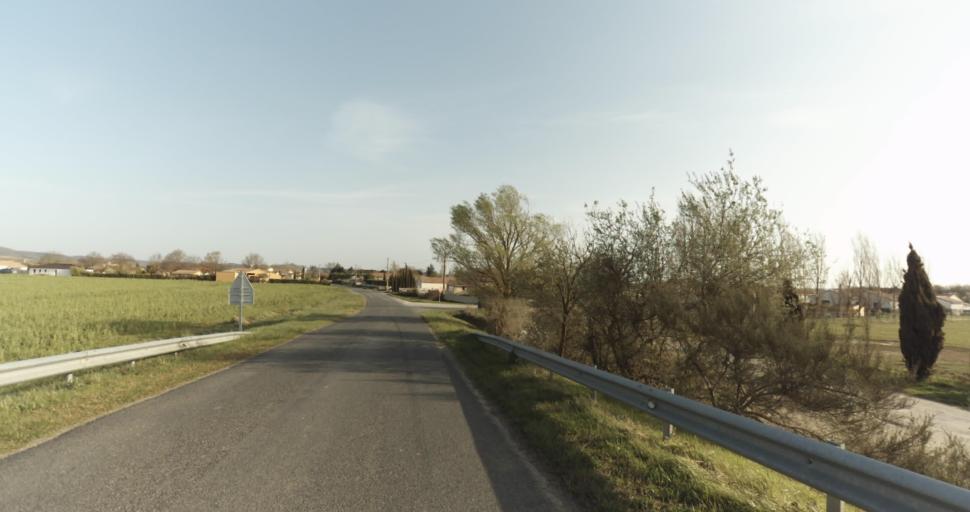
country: FR
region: Midi-Pyrenees
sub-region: Departement du Tarn
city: Saint-Sulpice-la-Pointe
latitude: 43.7550
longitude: 1.6874
